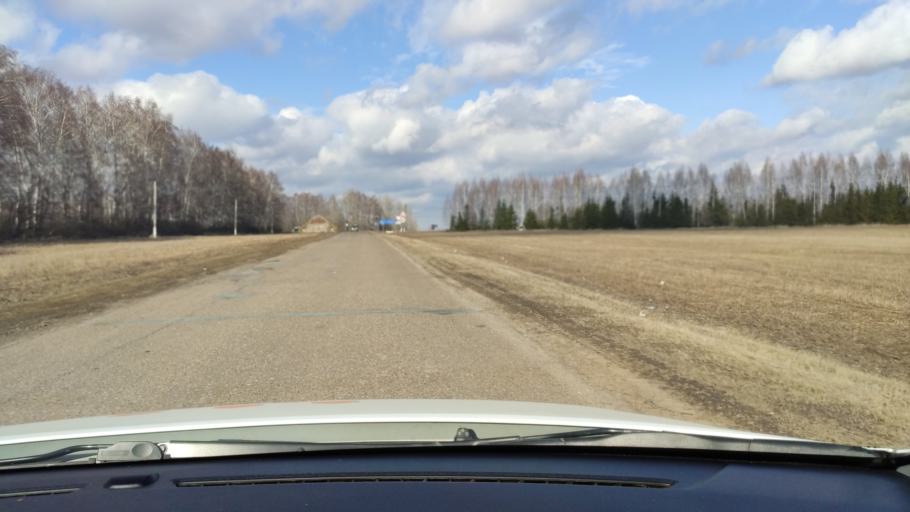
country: RU
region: Tatarstan
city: Vysokaya Gora
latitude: 56.0343
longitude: 49.2359
